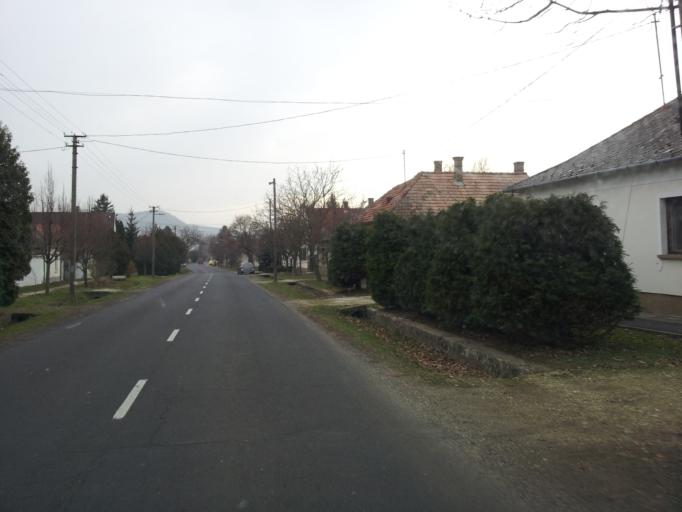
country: HU
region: Zala
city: Cserszegtomaj
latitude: 46.8914
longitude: 17.2288
